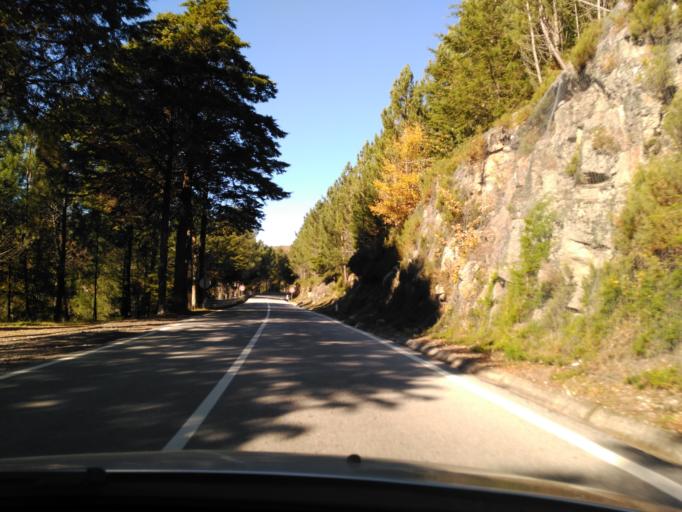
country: PT
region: Braga
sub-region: Cabeceiras de Basto
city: Cabeceiras de Basto
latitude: 41.6684
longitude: -7.9819
